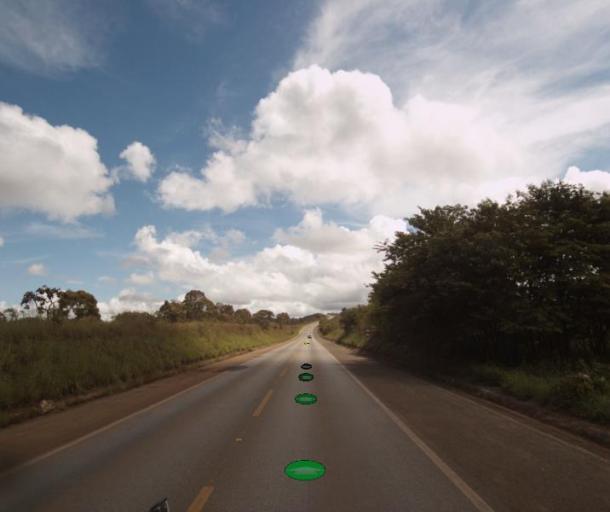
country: BR
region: Federal District
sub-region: Brasilia
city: Brasilia
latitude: -15.7434
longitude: -48.3669
